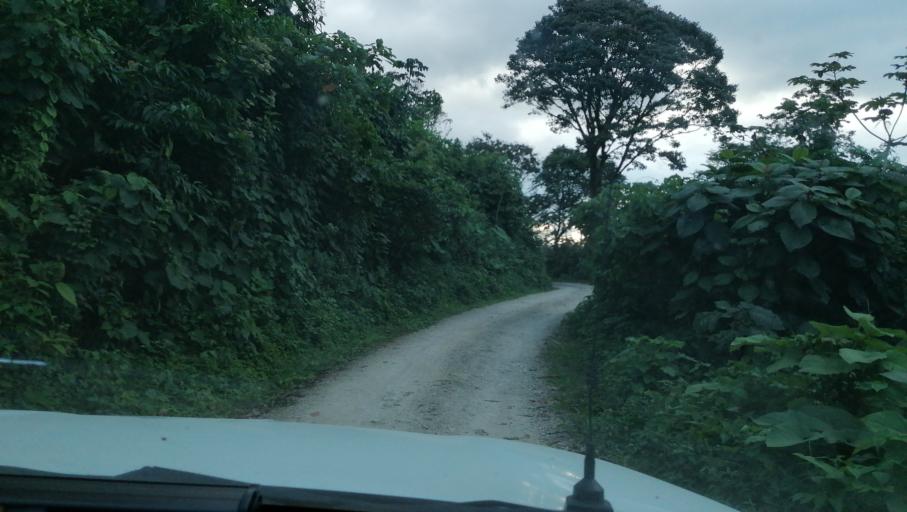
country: MX
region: Chiapas
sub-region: Francisco Leon
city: San Miguel la Sardina
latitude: 17.3092
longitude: -93.2678
